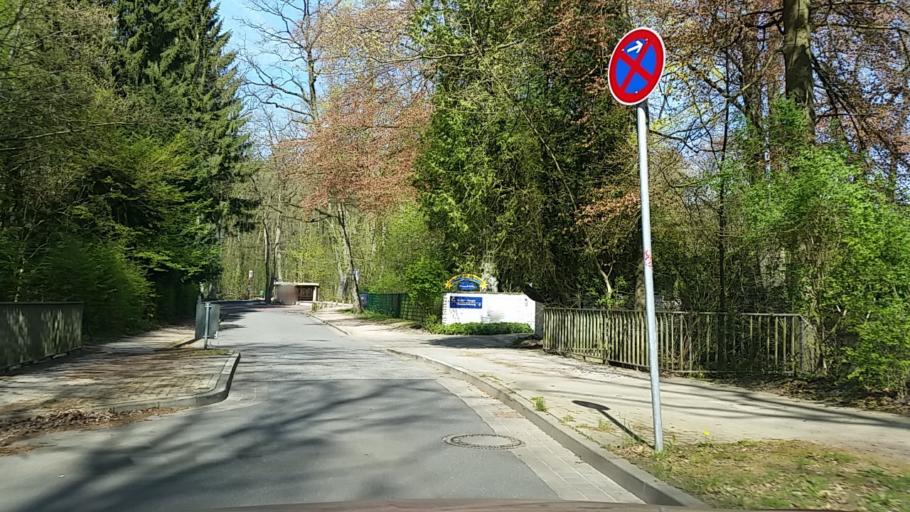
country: DE
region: Schleswig-Holstein
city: Wedel
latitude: 53.5893
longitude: 9.7526
